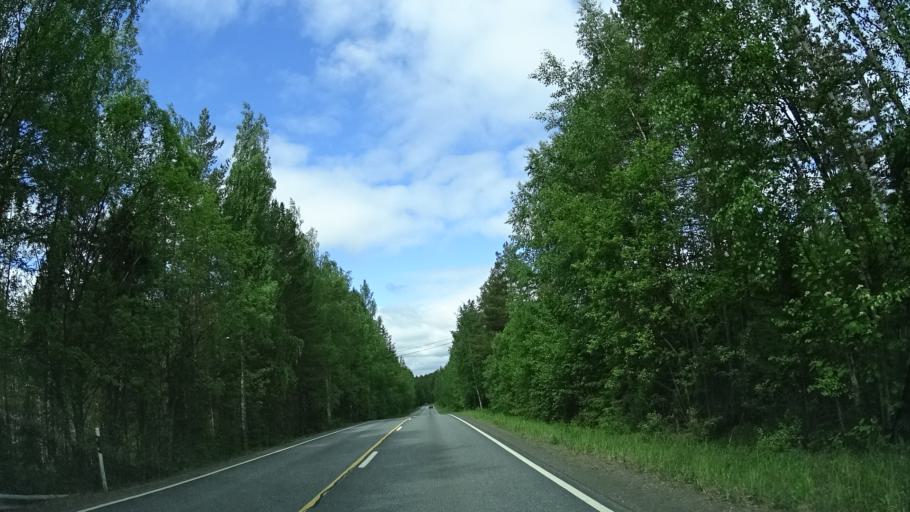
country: FI
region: Central Finland
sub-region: Jyvaeskylae
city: Korpilahti
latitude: 62.0057
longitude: 25.6723
